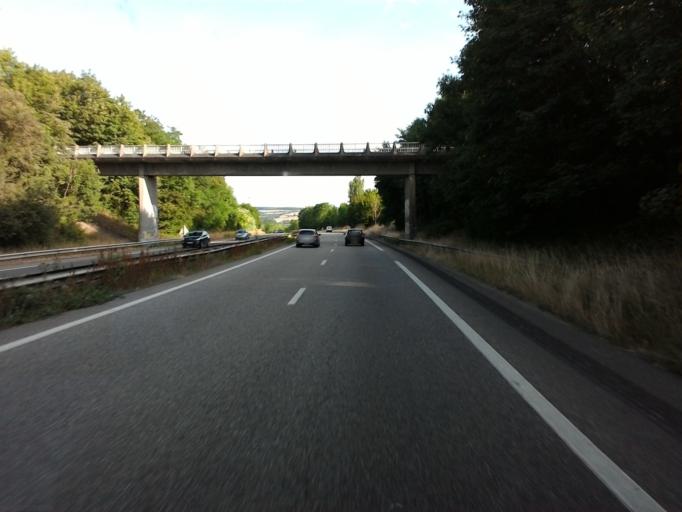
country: FR
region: Lorraine
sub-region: Departement de Meurthe-et-Moselle
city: Richardmenil
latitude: 48.5927
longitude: 6.1718
